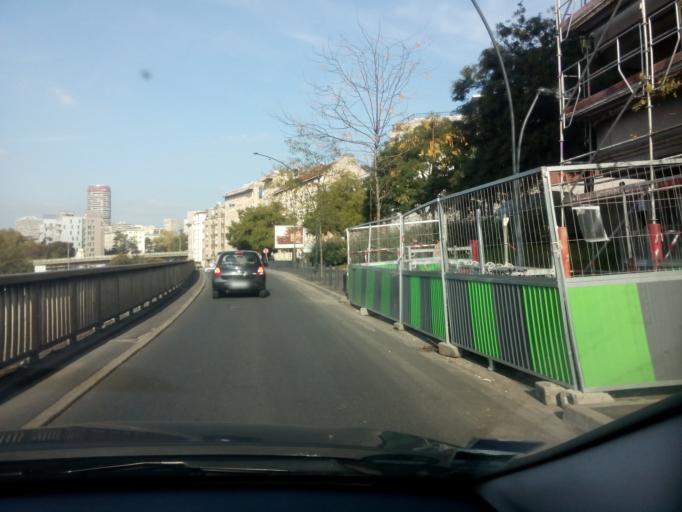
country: FR
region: Ile-de-France
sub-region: Departement du Val-de-Marne
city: Le Kremlin-Bicetre
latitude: 48.8141
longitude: 2.3555
